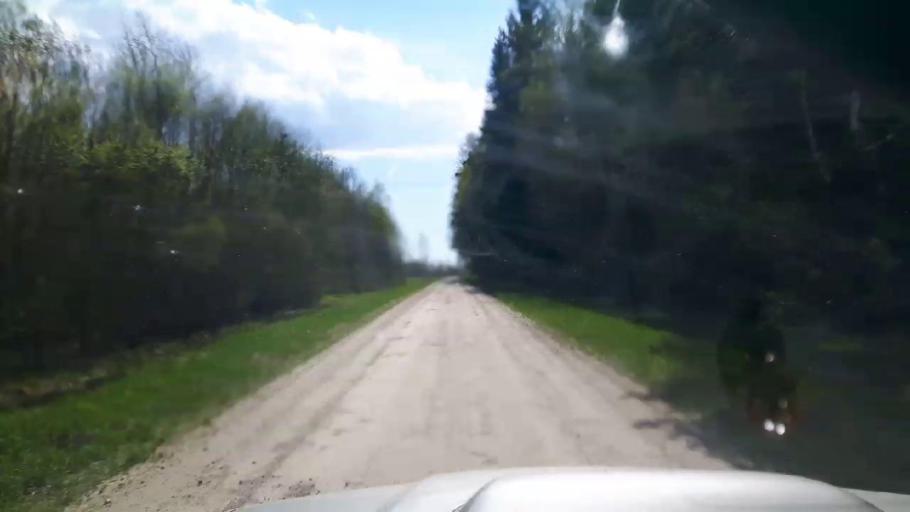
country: EE
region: Paernumaa
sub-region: Sindi linn
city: Sindi
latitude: 58.4274
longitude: 24.7661
